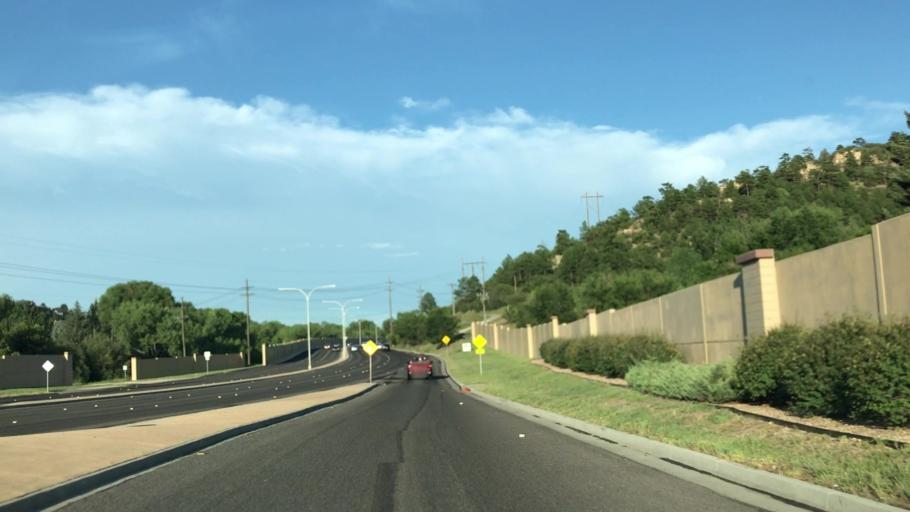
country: US
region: Colorado
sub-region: El Paso County
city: Colorado Springs
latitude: 38.8889
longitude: -104.7836
